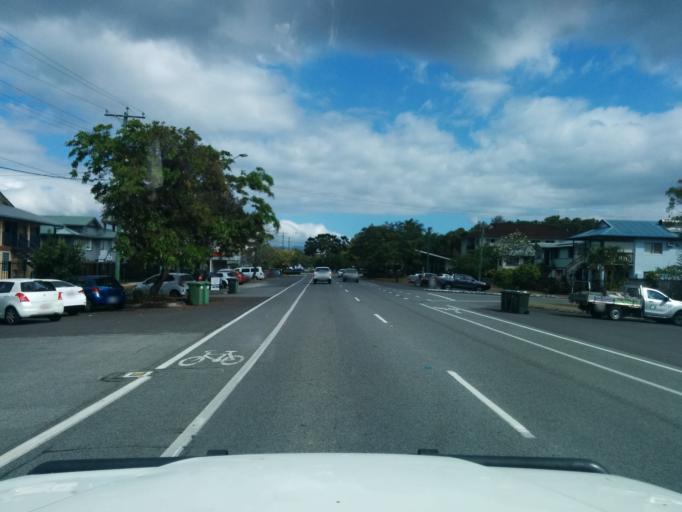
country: AU
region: Queensland
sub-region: Cairns
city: Cairns
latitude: -16.9130
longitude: 145.7631
